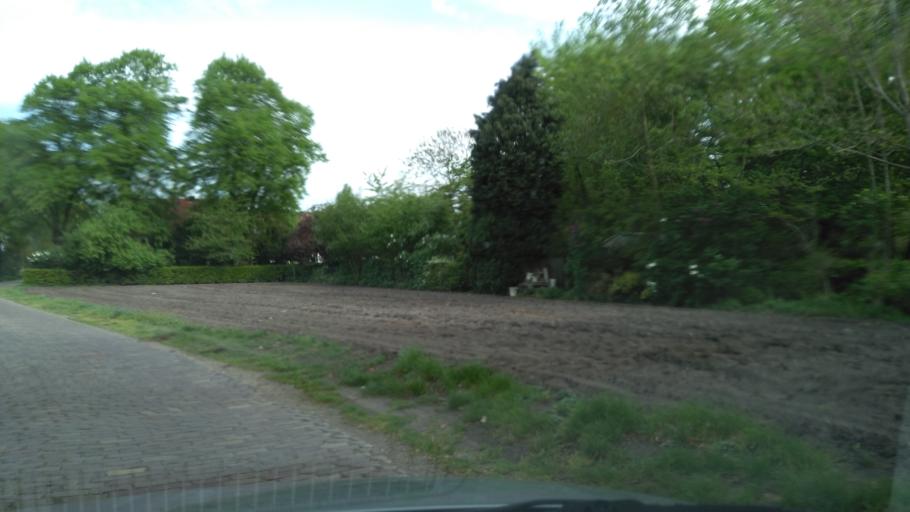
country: NL
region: North Brabant
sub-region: Gemeente Baarle-Nassau
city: Baarle-Nassau
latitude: 51.4305
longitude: 4.9288
